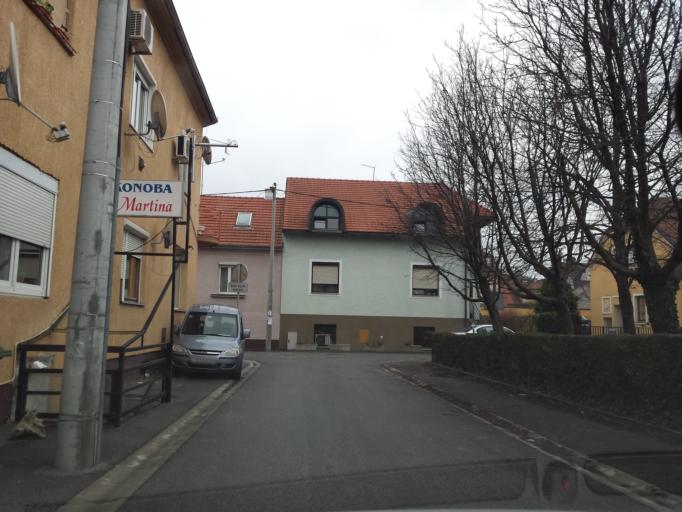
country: HR
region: Grad Zagreb
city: Zagreb - Centar
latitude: 45.8029
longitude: 15.9961
